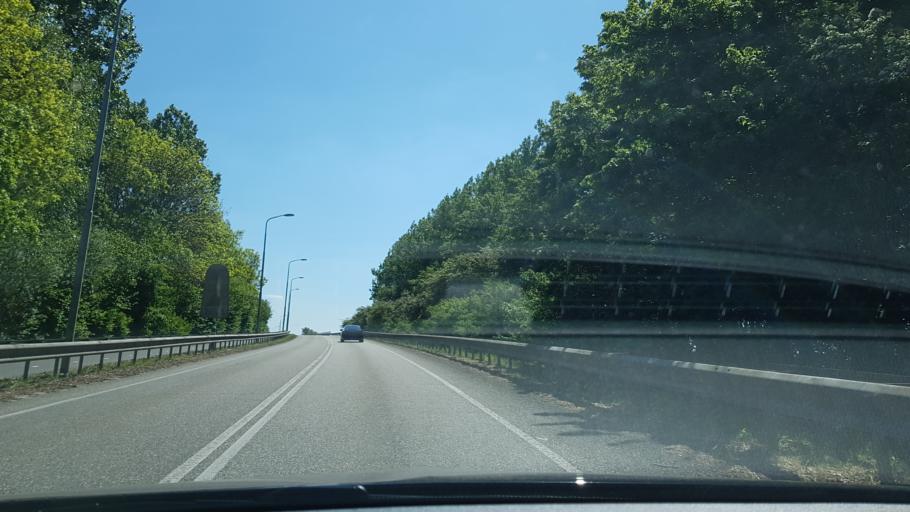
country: NL
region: North Holland
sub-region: Gemeente Haarlemmermeer
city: Hoofddorp
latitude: 52.2683
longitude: 4.6941
